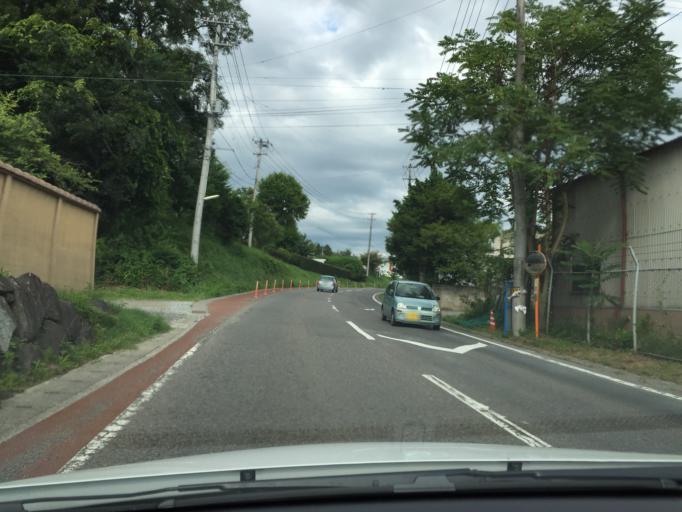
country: JP
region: Fukushima
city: Sukagawa
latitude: 37.2019
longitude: 140.3117
